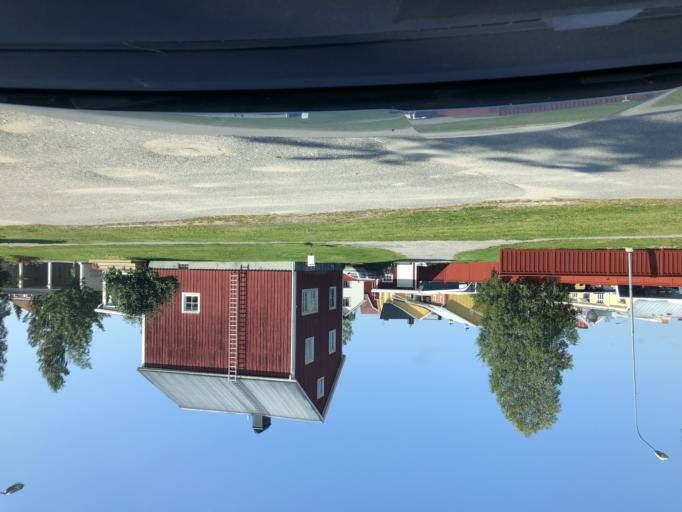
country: SE
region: Vaesternorrland
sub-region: OErnskoeldsviks Kommun
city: Bredbyn
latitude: 63.4484
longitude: 18.1059
